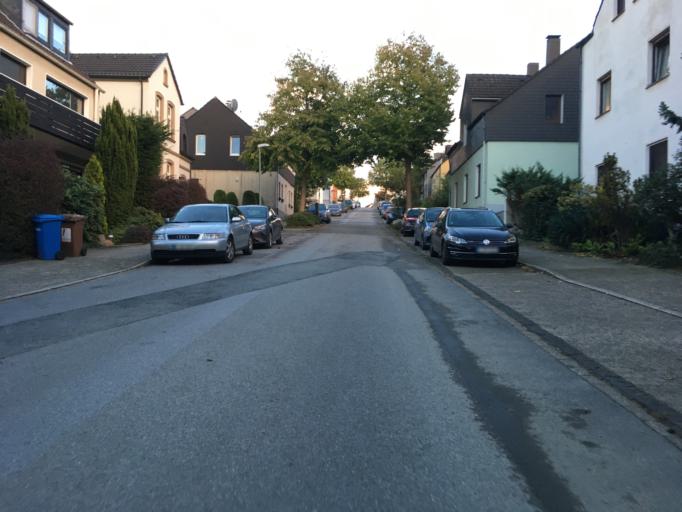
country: DE
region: North Rhine-Westphalia
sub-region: Regierungsbezirk Munster
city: Bottrop
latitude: 51.4829
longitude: 6.9278
